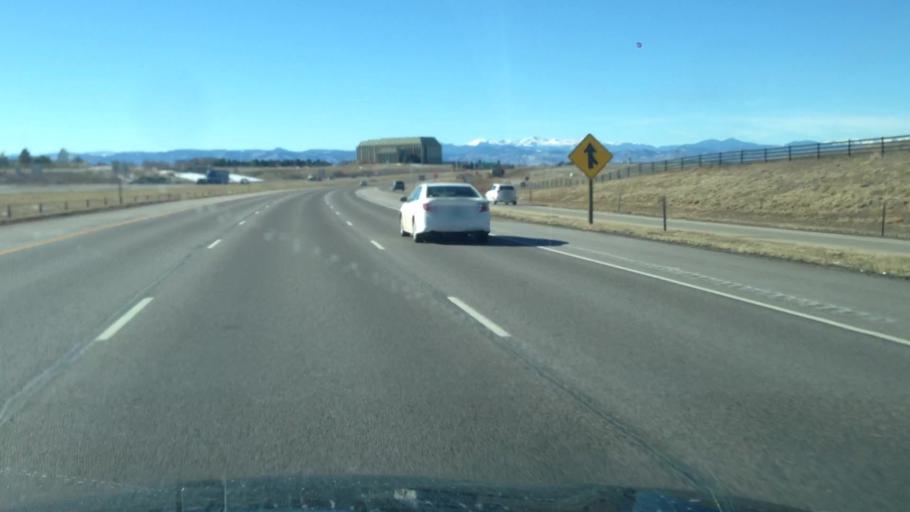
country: US
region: Colorado
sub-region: Douglas County
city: Meridian
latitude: 39.5511
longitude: -104.8446
